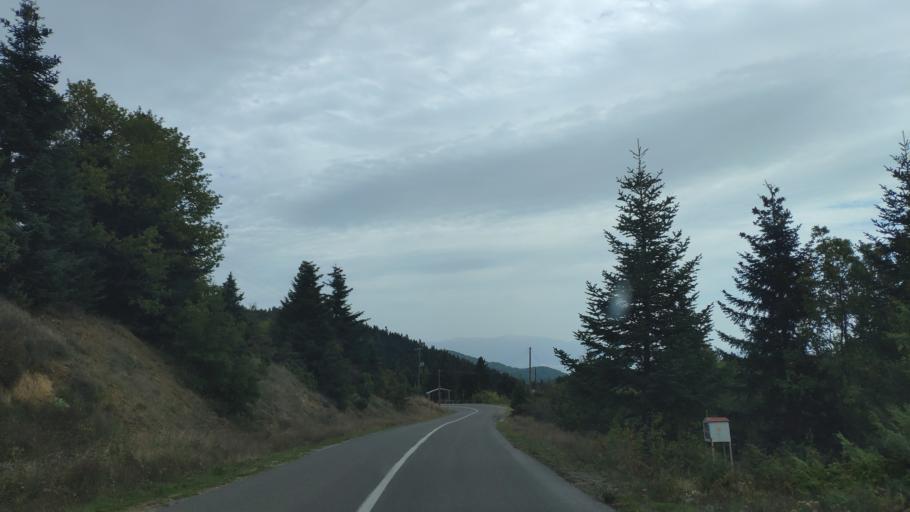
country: GR
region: Central Greece
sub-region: Nomos Fthiotidos
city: Stavros
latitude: 38.7279
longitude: 22.3379
